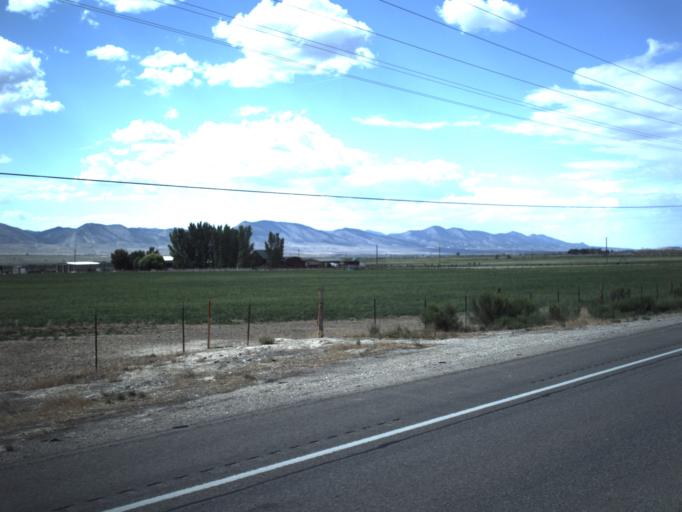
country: US
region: Utah
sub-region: Sanpete County
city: Centerfield
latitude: 39.0669
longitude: -111.8208
